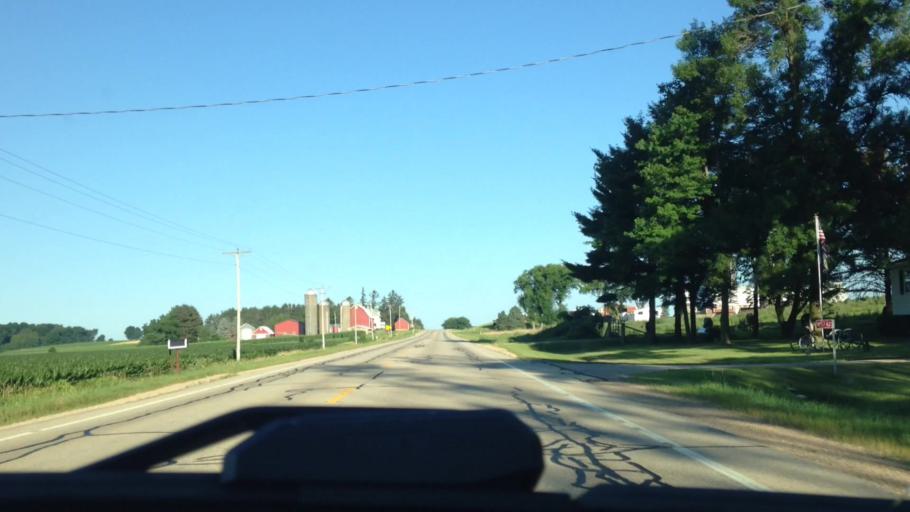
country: US
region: Wisconsin
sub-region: Dane County
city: De Forest
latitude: 43.3325
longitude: -89.2868
